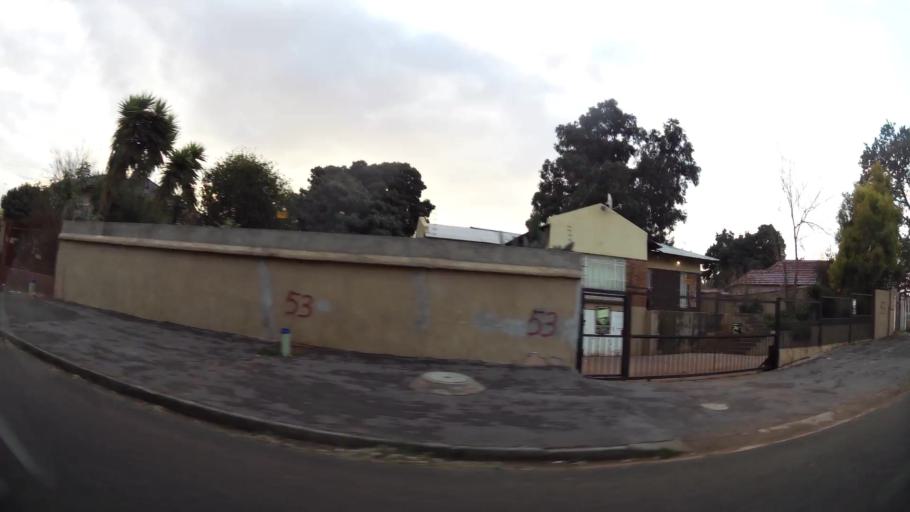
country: ZA
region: Gauteng
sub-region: Ekurhuleni Metropolitan Municipality
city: Germiston
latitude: -26.1893
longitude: 28.1520
